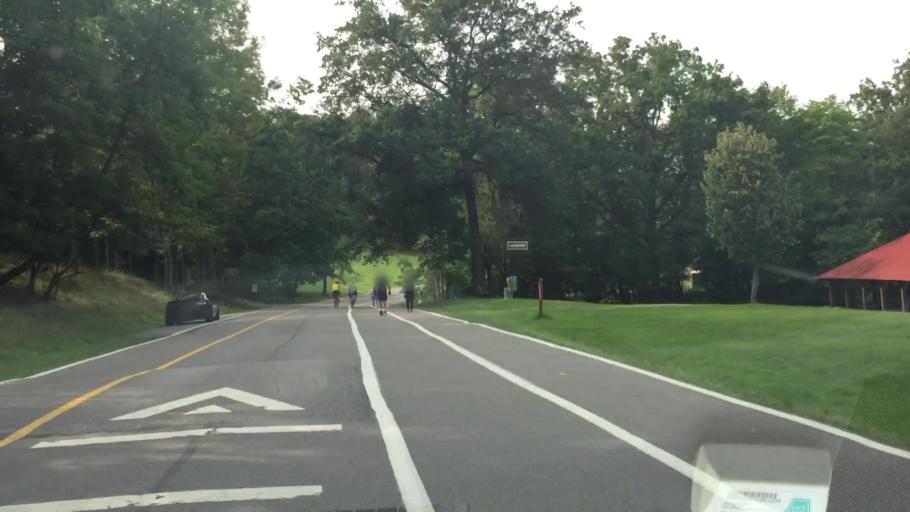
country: US
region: Pennsylvania
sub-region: Allegheny County
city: Gibsonia
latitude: 40.5999
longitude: -80.0042
